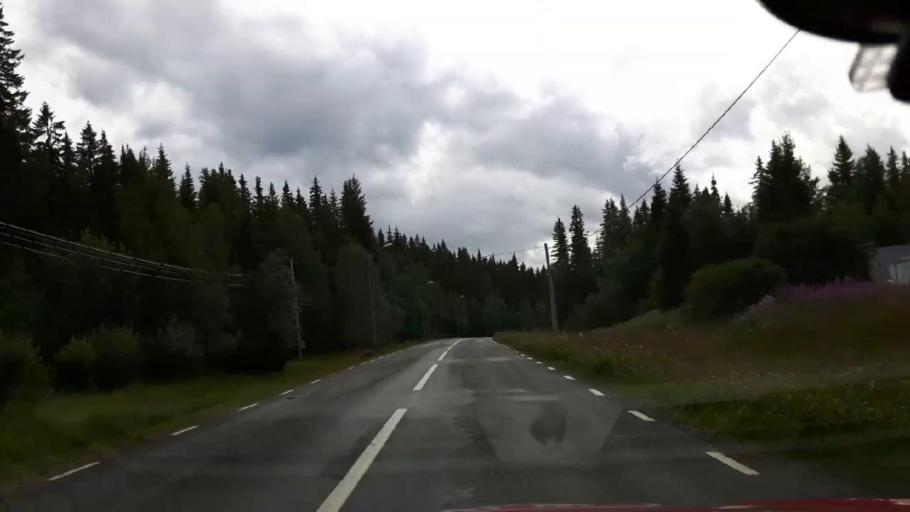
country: NO
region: Nord-Trondelag
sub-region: Lierne
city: Sandvika
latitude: 64.5043
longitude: 14.1571
